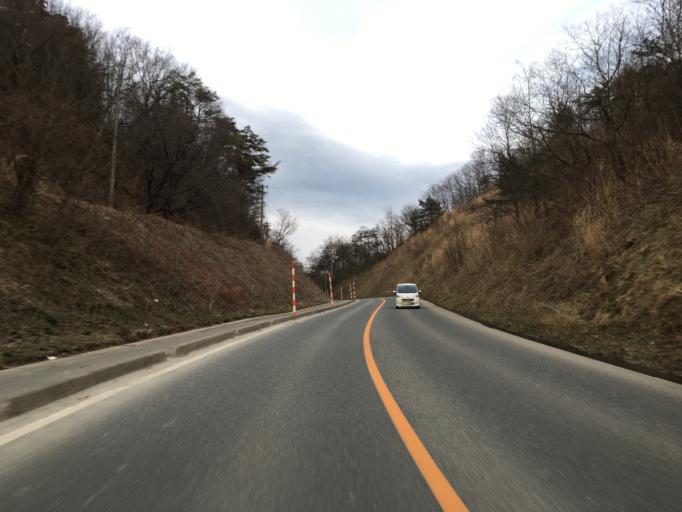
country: JP
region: Yamagata
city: Nagai
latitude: 38.0969
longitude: 140.0588
